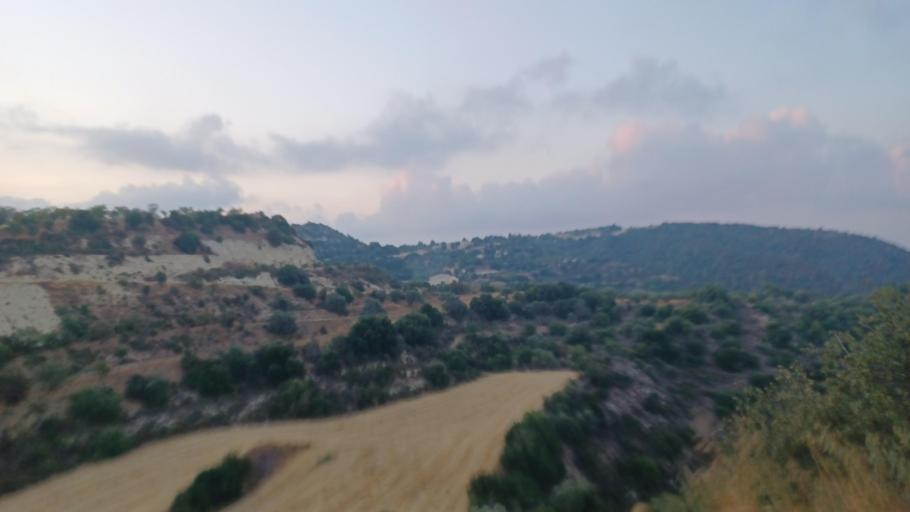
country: CY
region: Pafos
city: Mesogi
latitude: 34.8097
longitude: 32.5761
